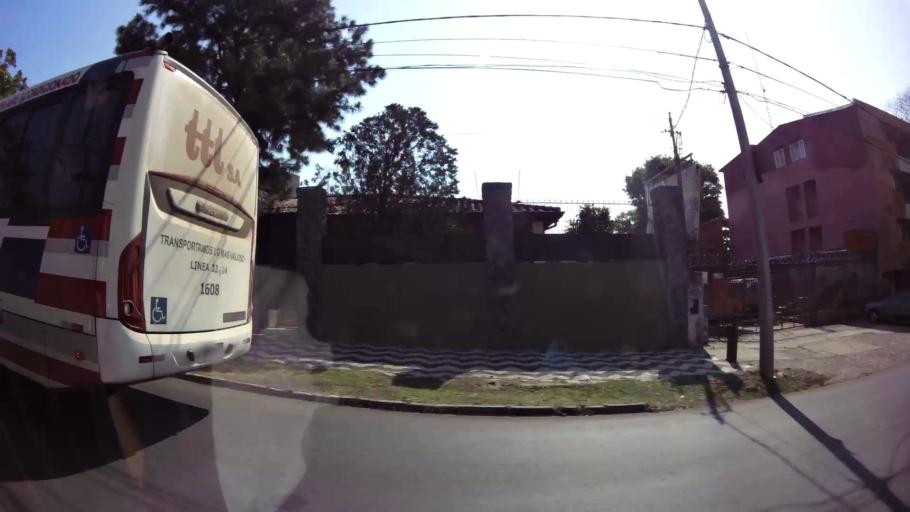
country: PY
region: Asuncion
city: Asuncion
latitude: -25.3170
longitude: -57.6299
